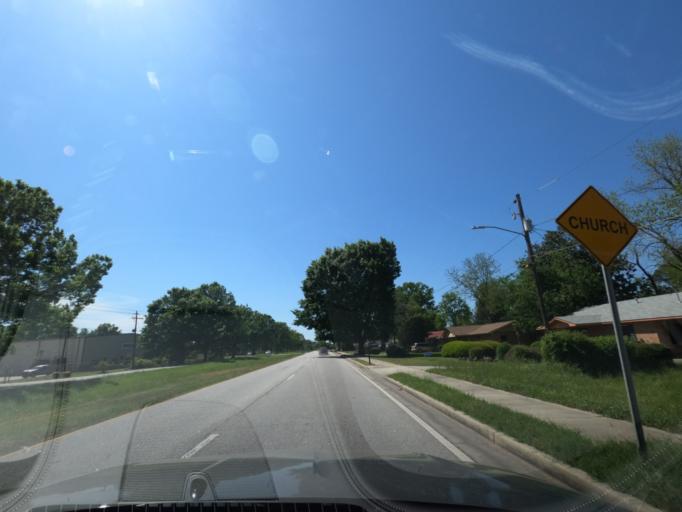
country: US
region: Georgia
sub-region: Richmond County
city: Augusta
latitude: 33.4562
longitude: -81.9432
